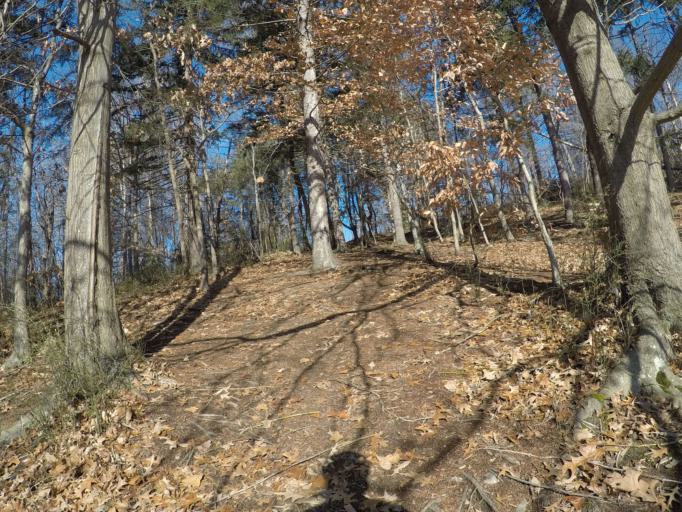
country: US
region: West Virginia
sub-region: Cabell County
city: Huntington
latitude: 38.4161
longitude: -82.3992
